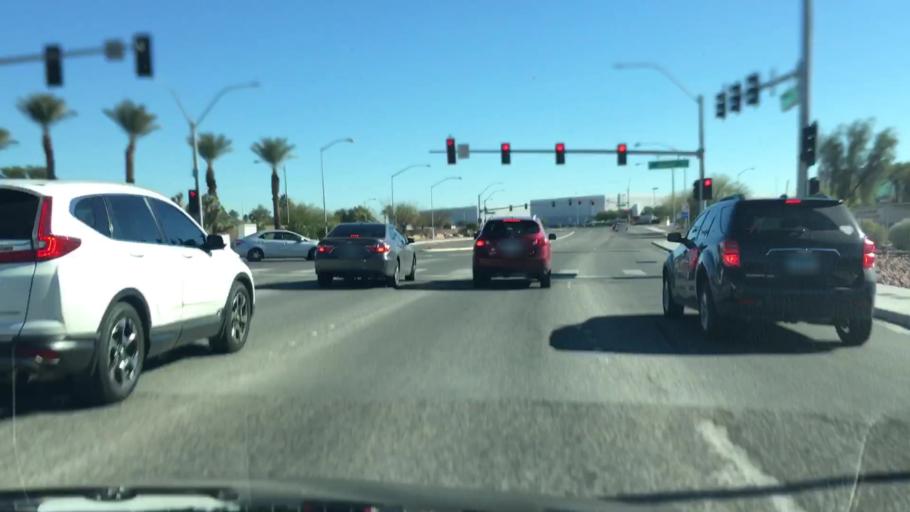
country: US
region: Nevada
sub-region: Clark County
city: Paradise
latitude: 36.0882
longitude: -115.1288
